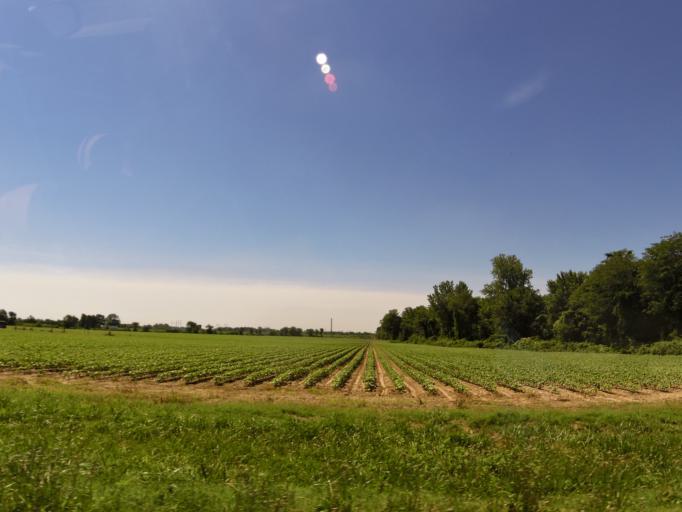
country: US
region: Missouri
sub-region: New Madrid County
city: Lilbourn
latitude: 36.5709
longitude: -89.5848
